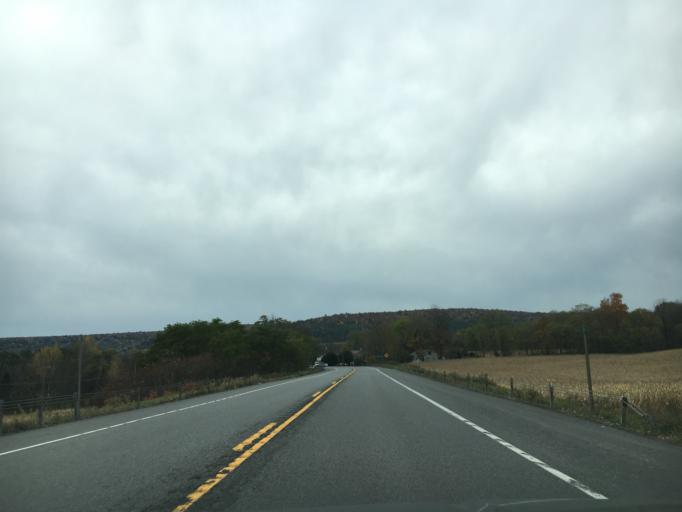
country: US
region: New York
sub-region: Otsego County
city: Oneonta
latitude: 42.5270
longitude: -74.9862
